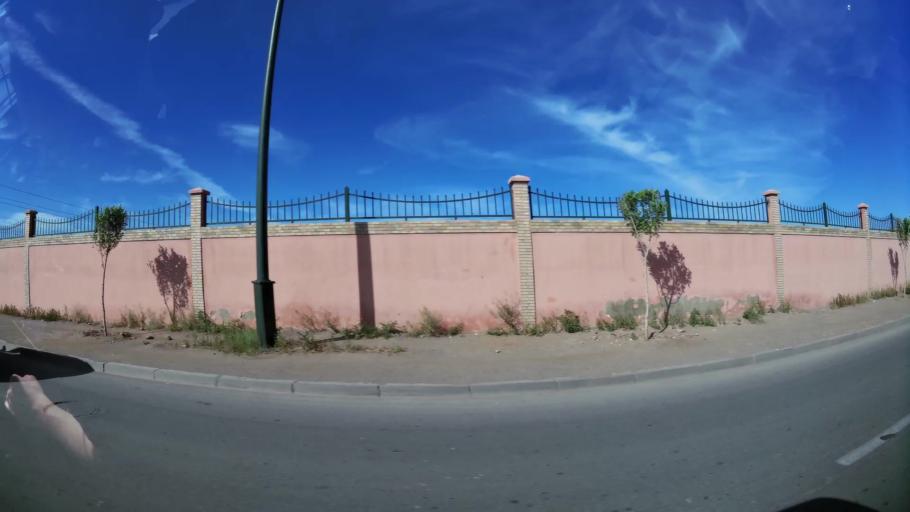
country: MA
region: Marrakech-Tensift-Al Haouz
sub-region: Marrakech
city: Marrakesh
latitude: 31.6603
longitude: -8.0263
